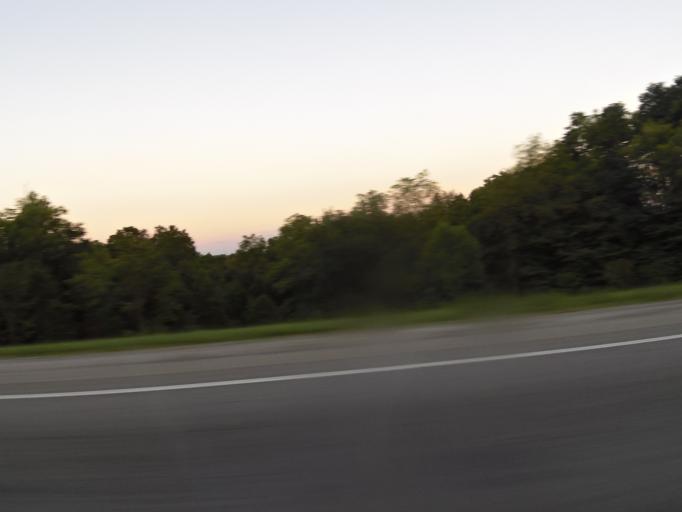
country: US
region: Kentucky
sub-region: Scott County
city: Georgetown
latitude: 38.3527
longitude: -84.5675
